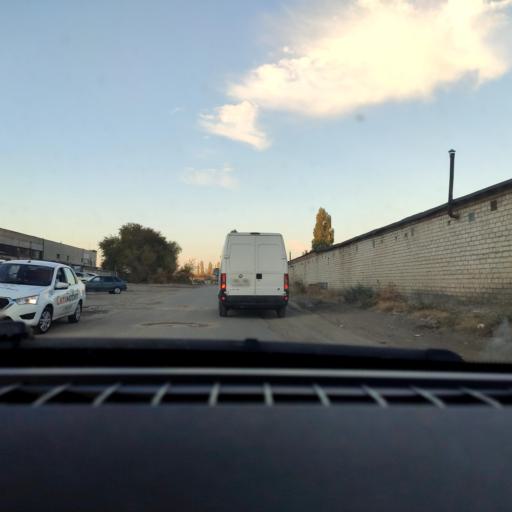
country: RU
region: Voronezj
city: Maslovka
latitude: 51.6388
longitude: 39.2796
